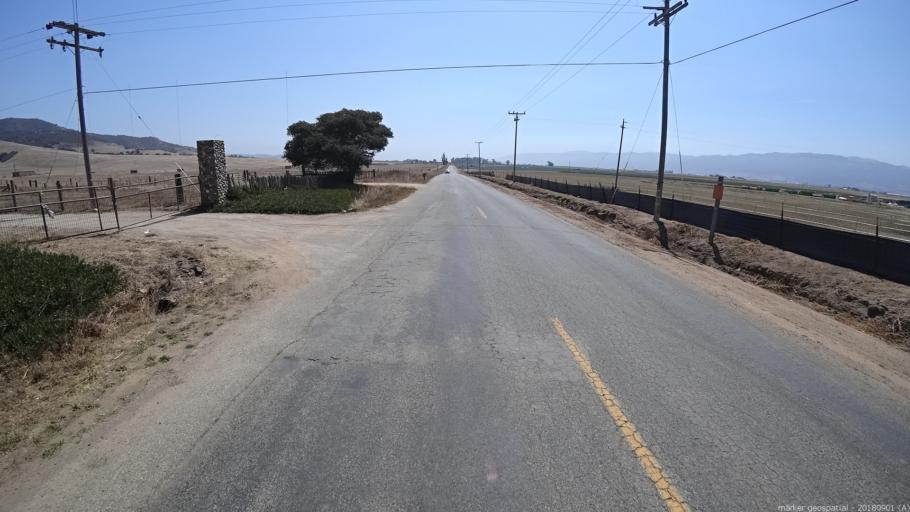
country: US
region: California
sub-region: Monterey County
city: Chualar
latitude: 36.6615
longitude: -121.5476
